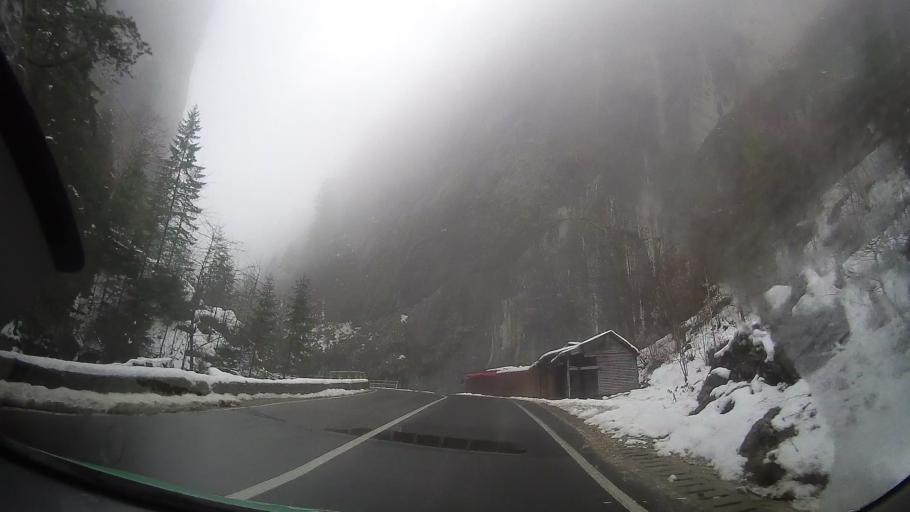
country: RO
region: Neamt
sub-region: Comuna Bicaz Chei
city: Bicaz Chei
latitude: 46.8134
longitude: 25.8271
